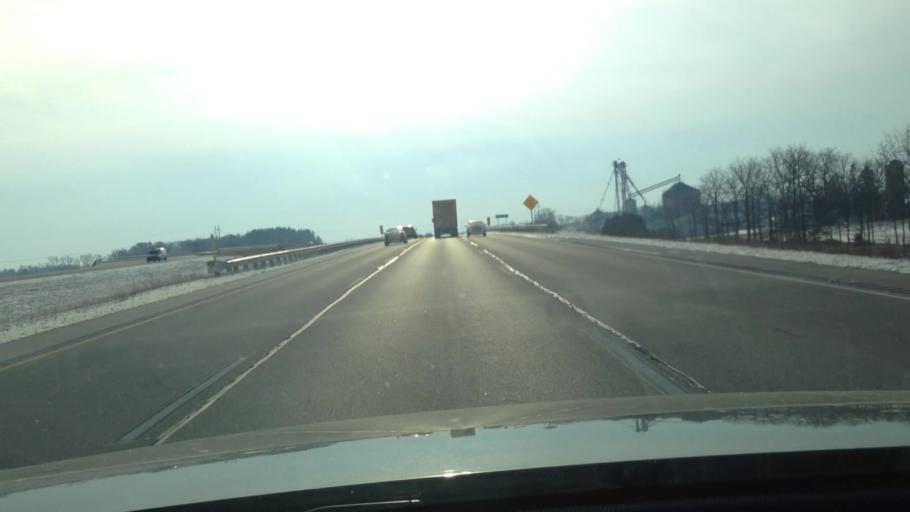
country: US
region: Wisconsin
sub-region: Walworth County
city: Elkhorn
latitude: 42.7075
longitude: -88.4833
